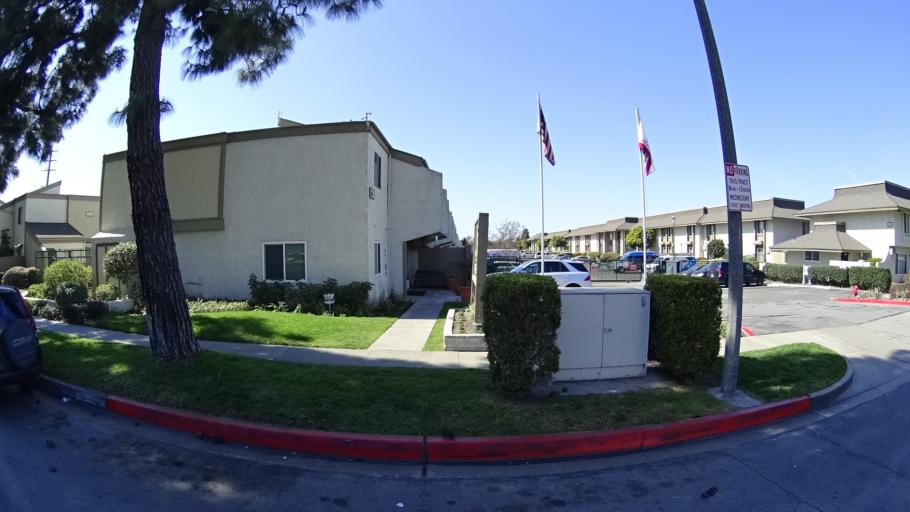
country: US
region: California
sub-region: Orange County
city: Anaheim
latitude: 33.8407
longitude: -117.9473
